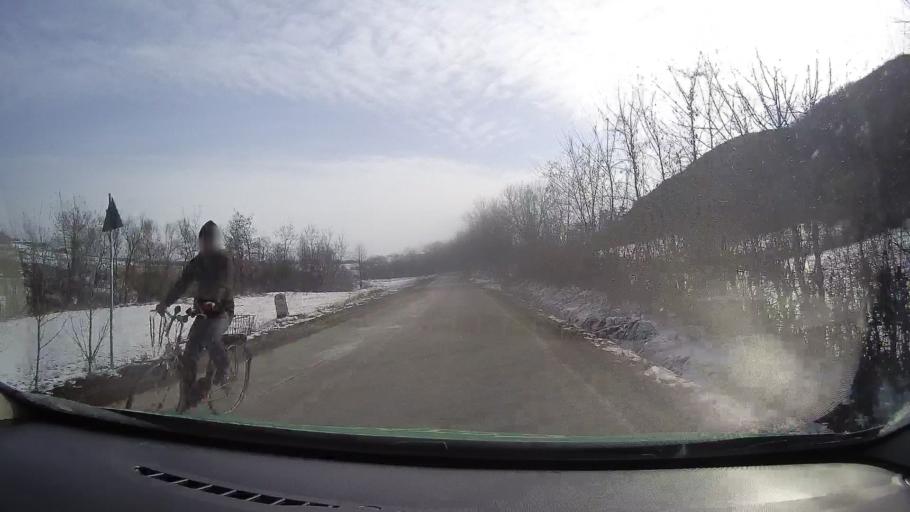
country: RO
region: Mures
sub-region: Comuna Apold
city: Saes
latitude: 46.1942
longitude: 24.7645
